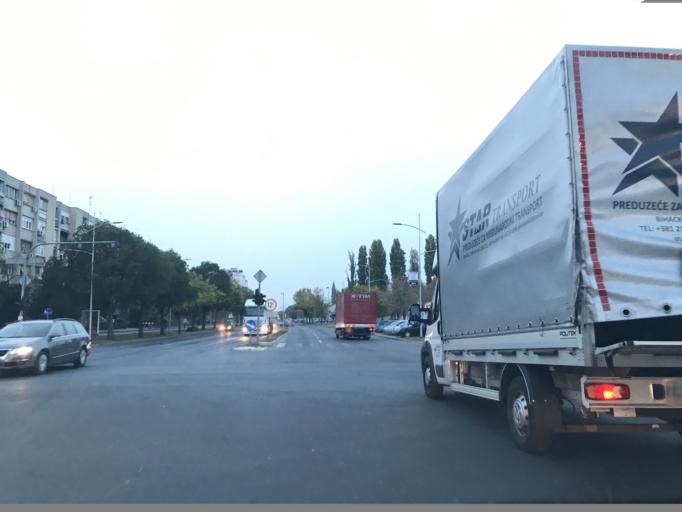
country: RS
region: Autonomna Pokrajina Vojvodina
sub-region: Juznobacki Okrug
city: Novi Sad
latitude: 45.2641
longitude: 19.8172
